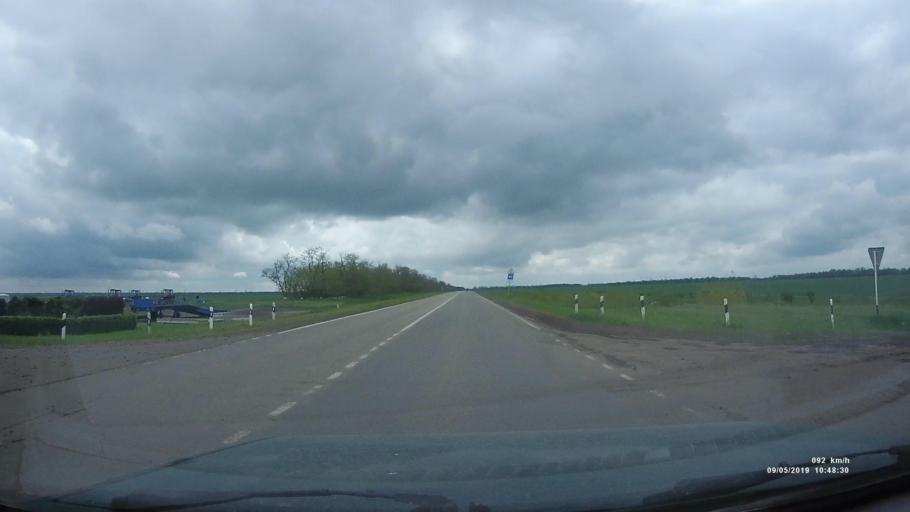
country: RU
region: Rostov
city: Peshkovo
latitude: 46.9557
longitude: 39.3556
